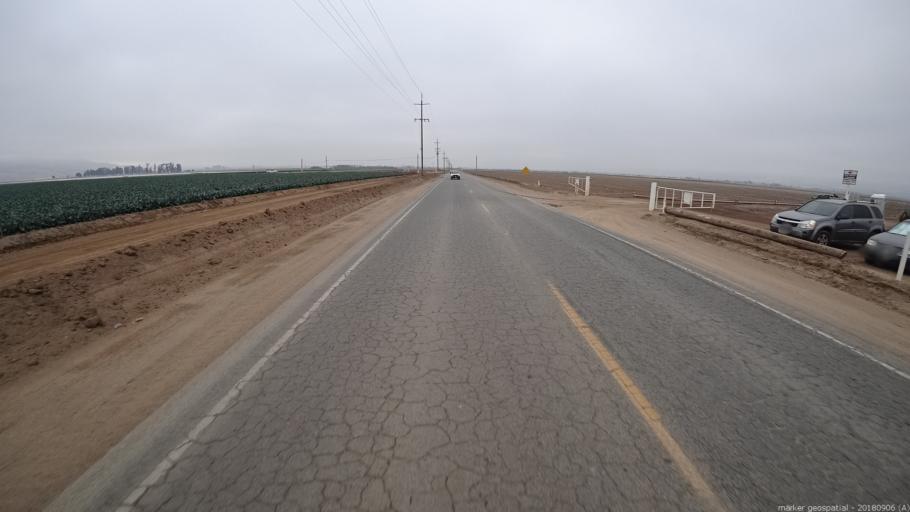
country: US
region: California
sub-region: Monterey County
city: Salinas
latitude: 36.6562
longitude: -121.5864
